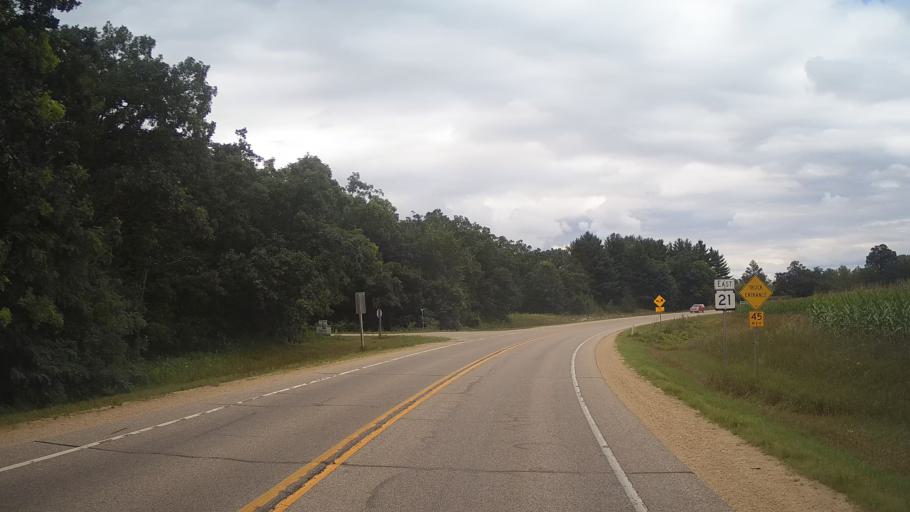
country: US
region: Wisconsin
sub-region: Waushara County
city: Wautoma
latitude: 44.0673
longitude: -89.3638
